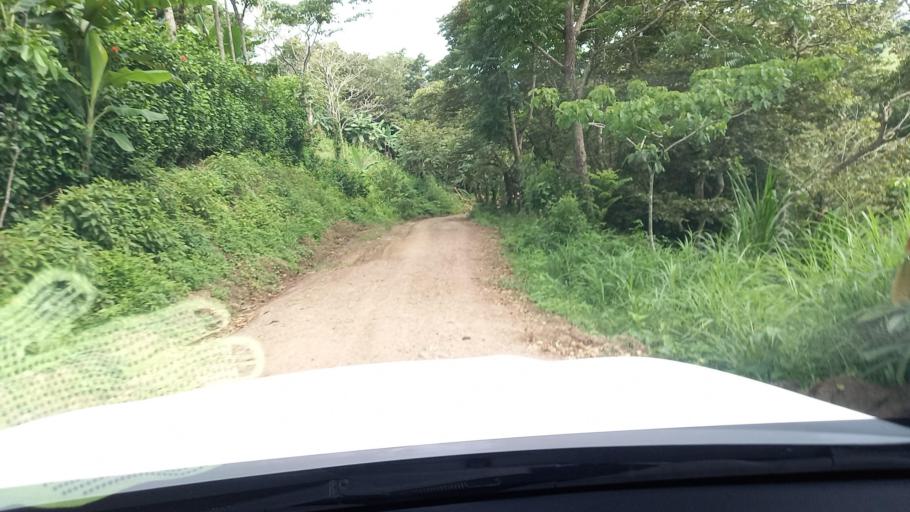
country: NI
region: Jinotega
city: San Jose de Bocay
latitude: 13.4046
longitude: -85.7014
